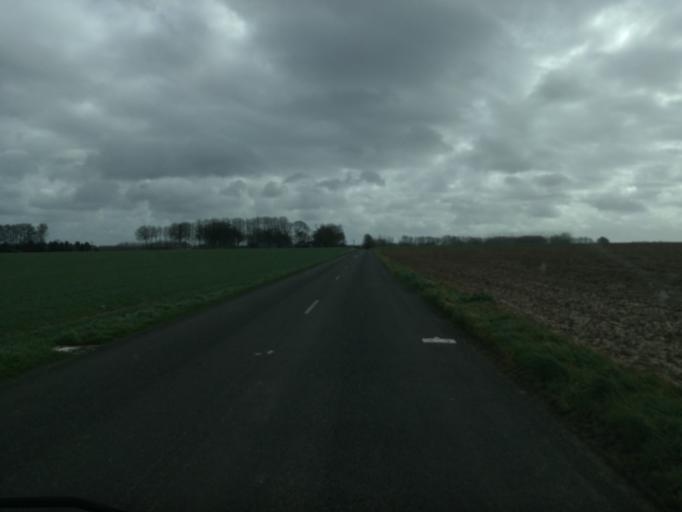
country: FR
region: Haute-Normandie
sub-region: Departement de la Seine-Maritime
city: Yebleron
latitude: 49.6598
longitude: 0.5148
